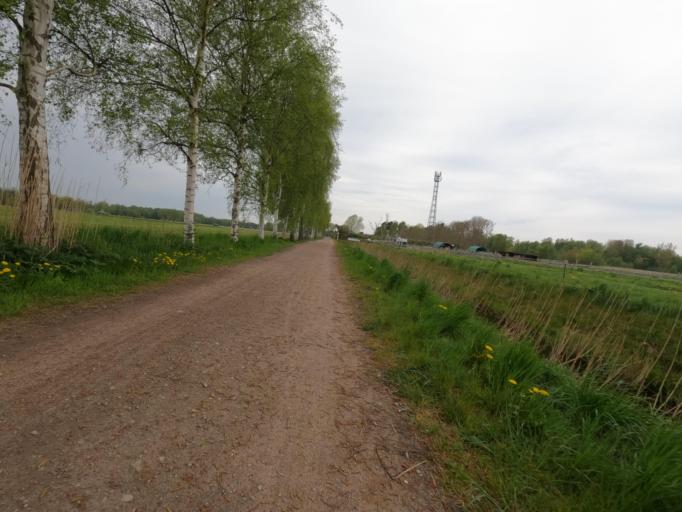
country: DE
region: Mecklenburg-Vorpommern
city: Ostseebad Dierhagen
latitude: 54.2964
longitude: 12.3546
